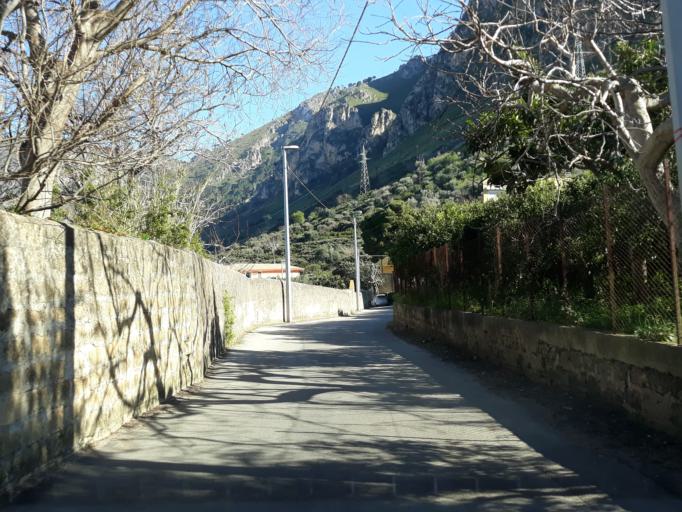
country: IT
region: Sicily
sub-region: Palermo
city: Villa Ciambra
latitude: 38.0762
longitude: 13.3490
